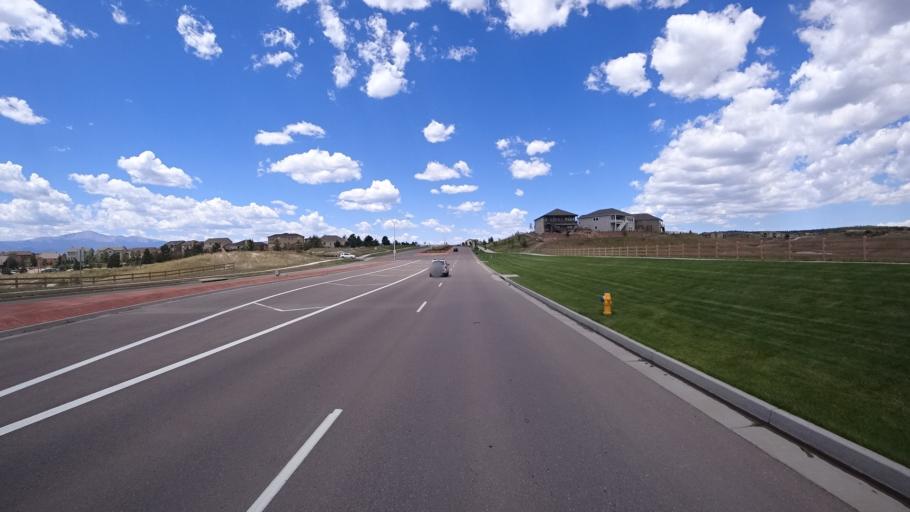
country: US
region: Colorado
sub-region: El Paso County
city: Black Forest
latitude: 38.9606
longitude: -104.7104
